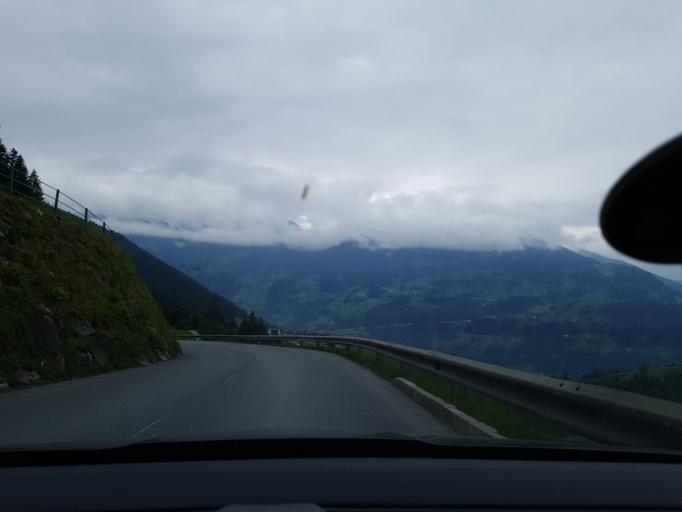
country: AT
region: Tyrol
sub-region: Politischer Bezirk Schwaz
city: Hainzenberg
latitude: 47.2145
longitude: 11.9148
